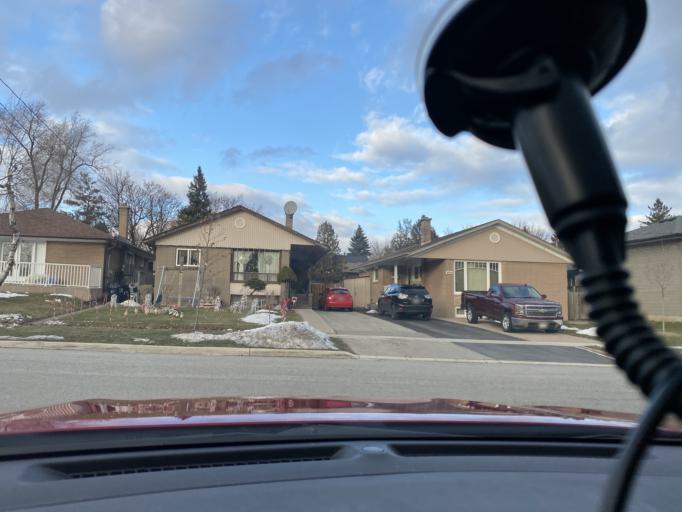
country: CA
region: Ontario
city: Scarborough
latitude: 43.7684
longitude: -79.2108
